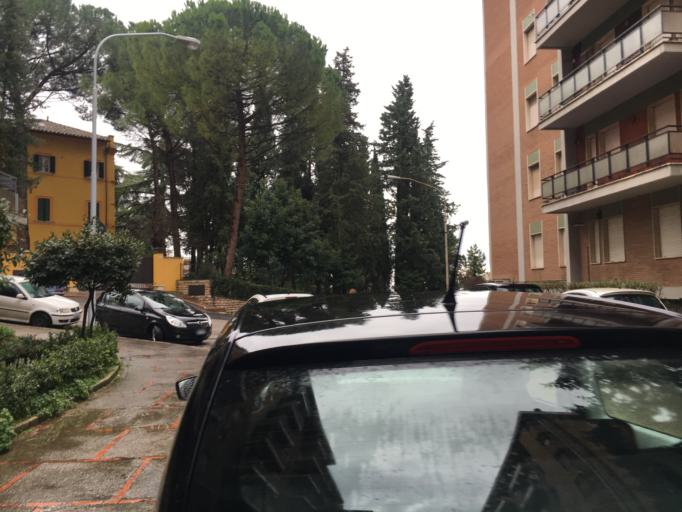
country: IT
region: Umbria
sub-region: Provincia di Perugia
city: Perugia
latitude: 43.1127
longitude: 12.3792
